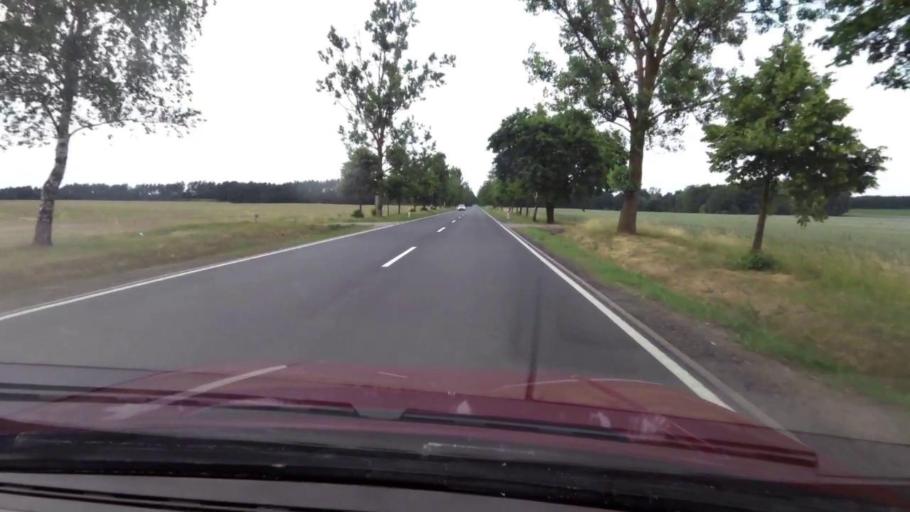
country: PL
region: Pomeranian Voivodeship
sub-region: Powiat bytowski
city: Trzebielino
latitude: 54.2616
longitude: 17.1017
